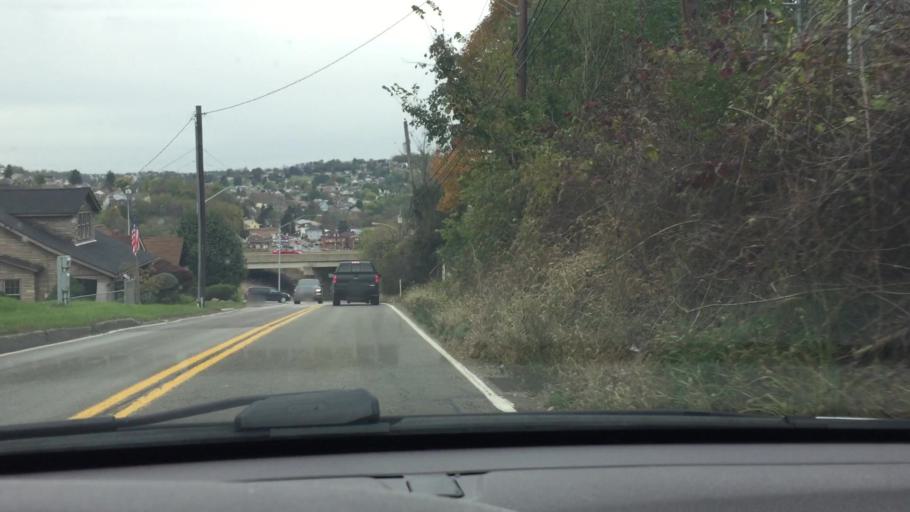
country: US
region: Pennsylvania
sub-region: Washington County
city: Canonsburg
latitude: 40.2578
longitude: -80.1746
